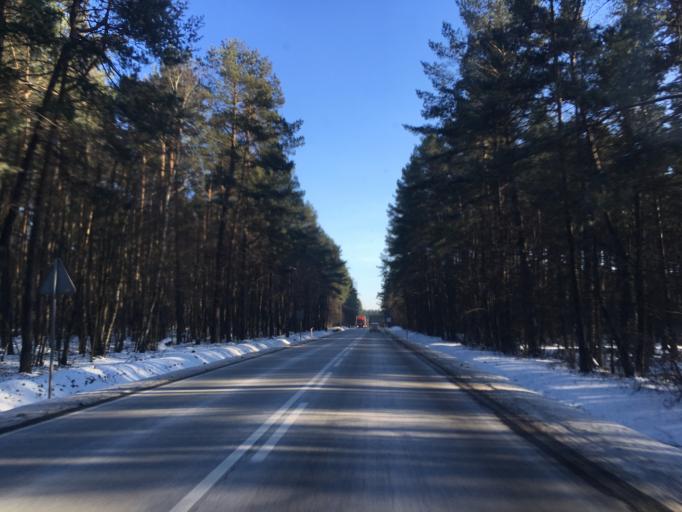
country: PL
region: Pomeranian Voivodeship
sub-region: Powiat koscierski
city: Koscierzyna
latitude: 54.1232
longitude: 17.8815
